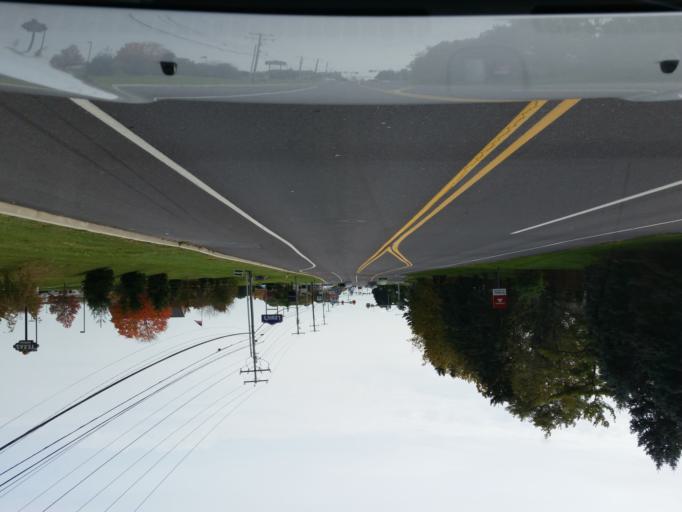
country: US
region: Pennsylvania
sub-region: Lebanon County
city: Palmyra
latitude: 40.3198
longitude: -76.5633
